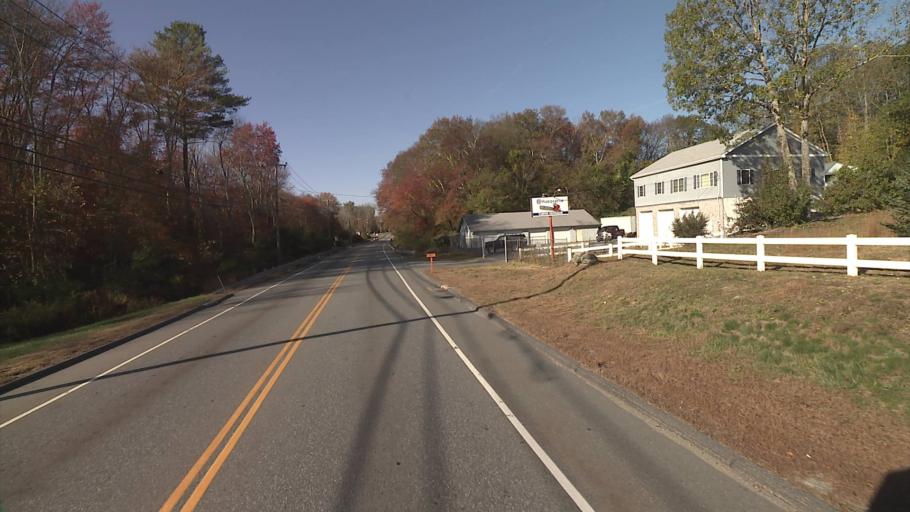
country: US
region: Connecticut
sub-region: Windham County
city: East Brooklyn
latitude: 41.7940
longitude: -71.9394
